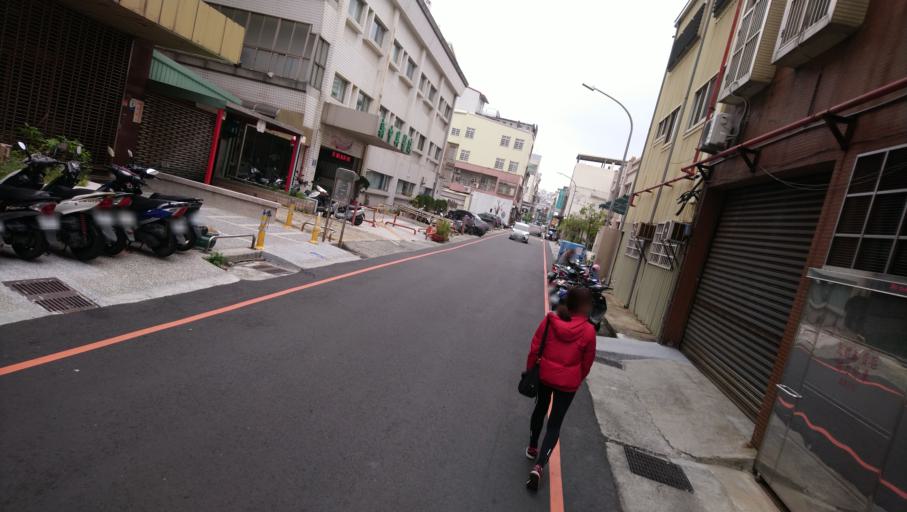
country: TW
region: Taiwan
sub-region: Hsinchu
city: Hsinchu
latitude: 24.8016
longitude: 120.9631
